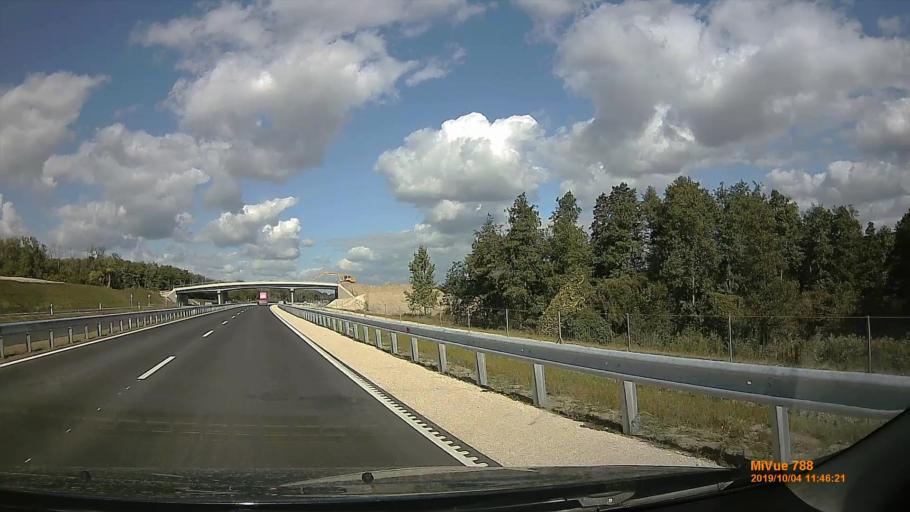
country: HU
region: Somogy
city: Karad
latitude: 46.6361
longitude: 17.7900
